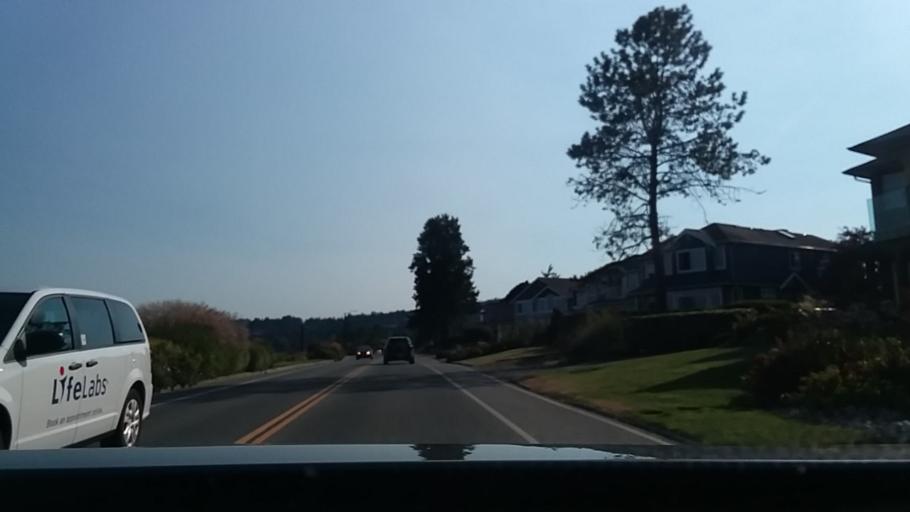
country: CA
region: British Columbia
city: North Saanich
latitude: 48.6392
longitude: -123.4023
